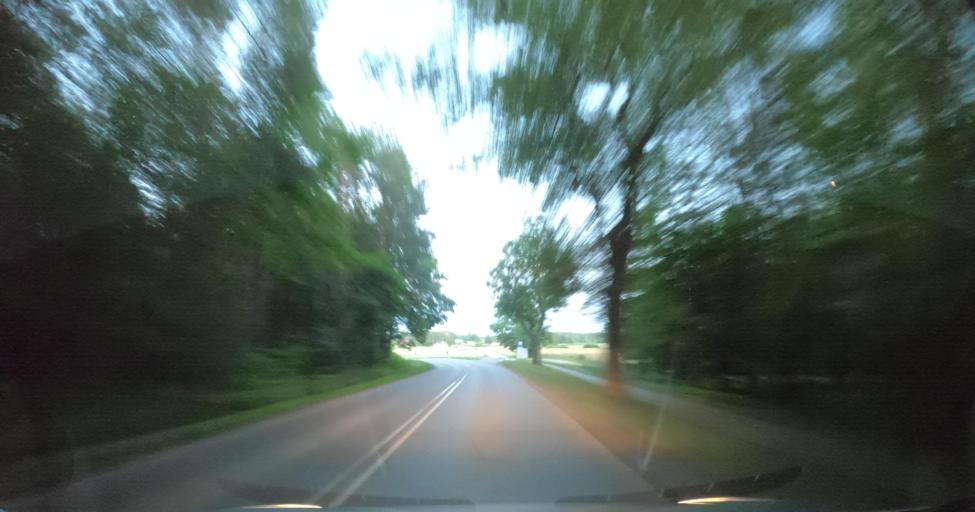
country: PL
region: Pomeranian Voivodeship
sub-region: Powiat wejherowski
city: Szemud
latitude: 54.4674
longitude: 18.2816
